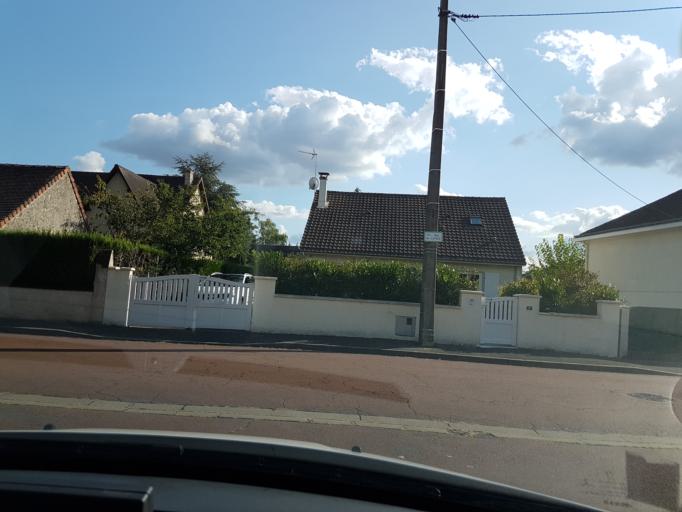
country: FR
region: Centre
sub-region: Departement d'Indre-et-Loire
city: Saint-Avertin
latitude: 47.3663
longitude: 0.7507
